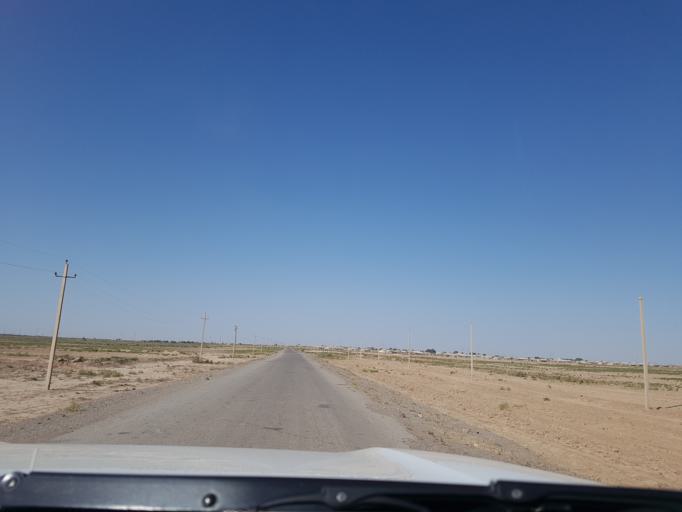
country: IR
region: Razavi Khorasan
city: Sarakhs
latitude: 36.4994
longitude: 61.2537
